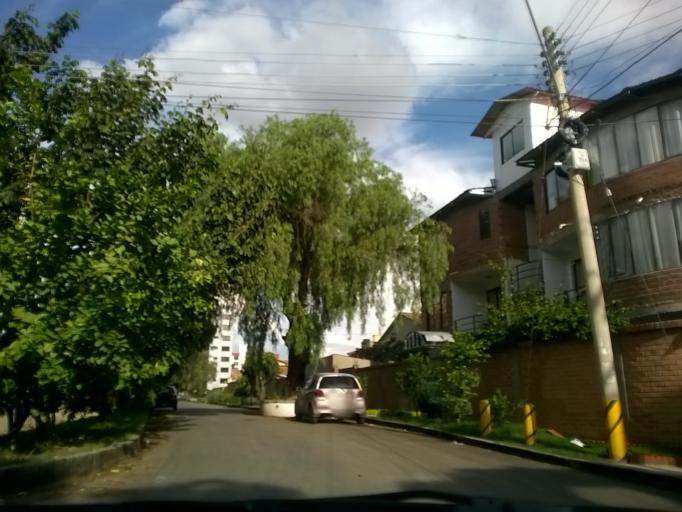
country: BO
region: Cochabamba
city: Cochabamba
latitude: -17.3655
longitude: -66.1809
